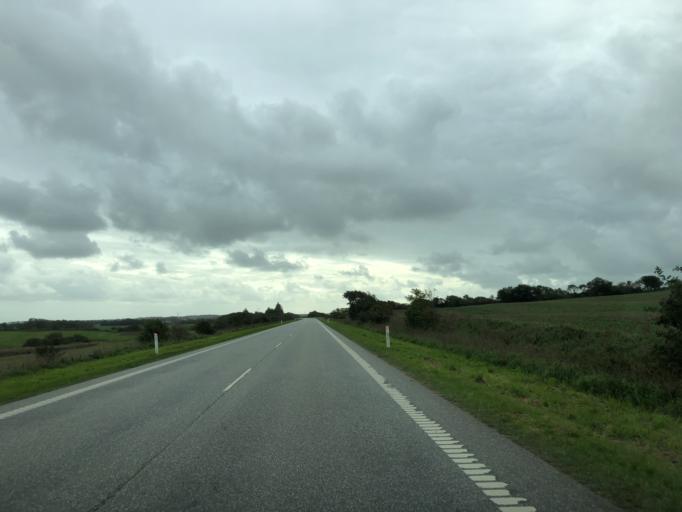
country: DK
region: North Denmark
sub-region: Thisted Kommune
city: Hurup
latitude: 56.8047
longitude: 8.4772
